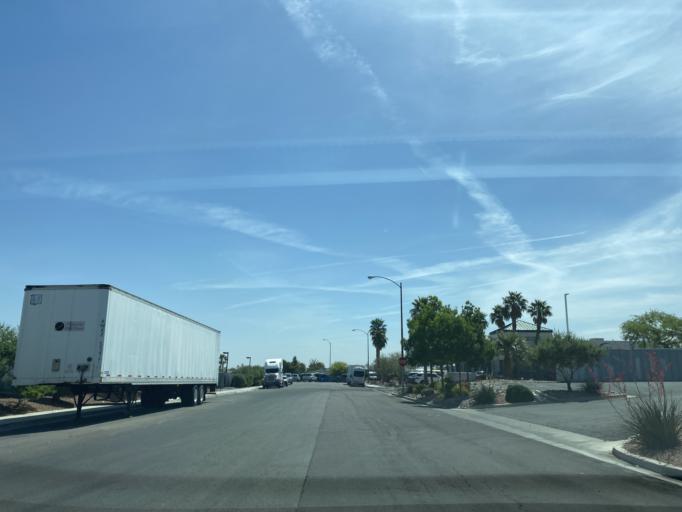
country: US
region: Nevada
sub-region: Clark County
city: Paradise
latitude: 36.0749
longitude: -115.1776
